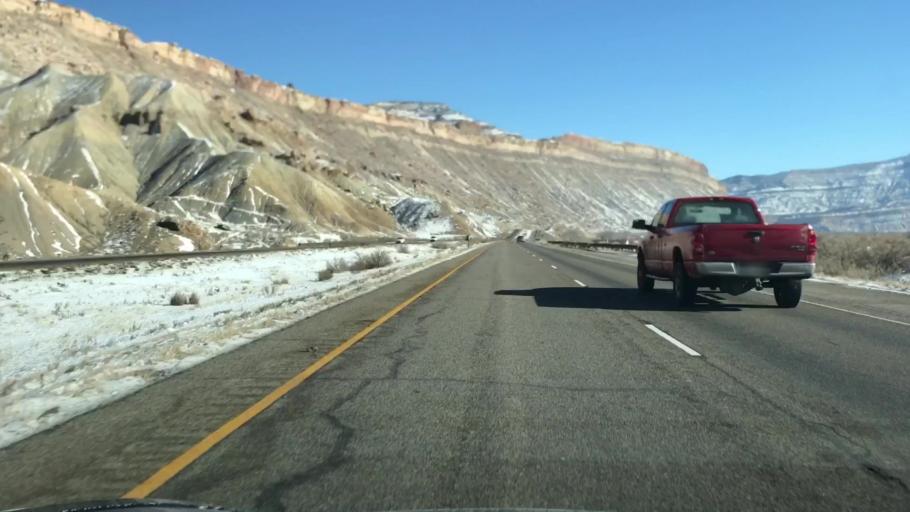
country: US
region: Colorado
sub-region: Mesa County
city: Palisade
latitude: 39.1166
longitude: -108.3934
